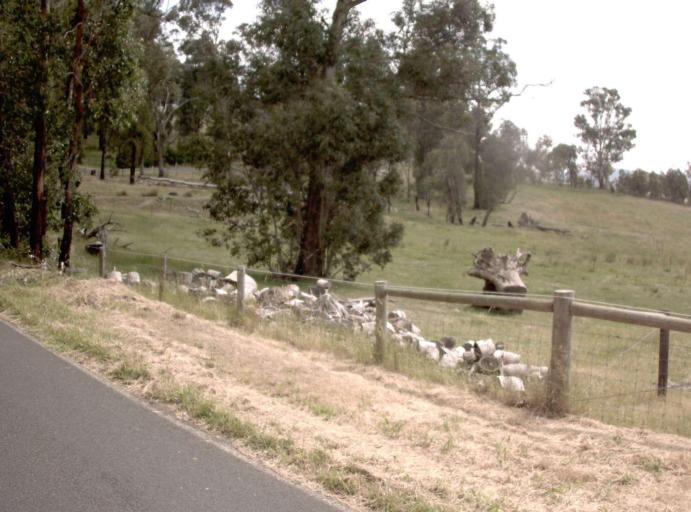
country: AU
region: Victoria
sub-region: Latrobe
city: Traralgon
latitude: -38.3175
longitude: 146.5735
